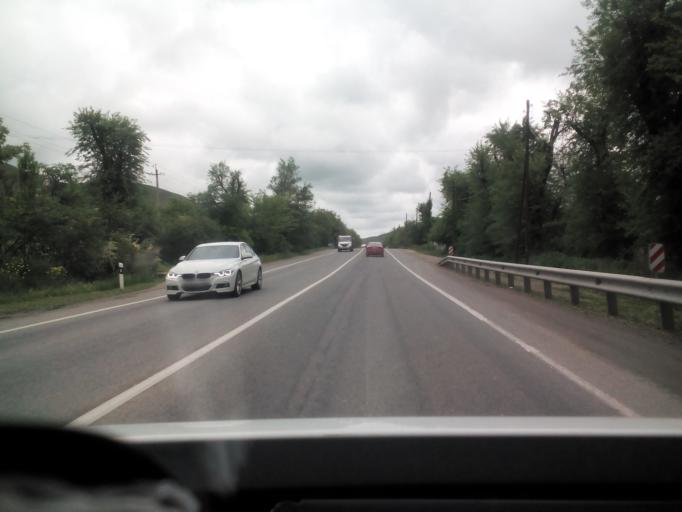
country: RU
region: Stavropol'skiy
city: Yasnaya Polyana
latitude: 43.9679
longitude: 42.7797
